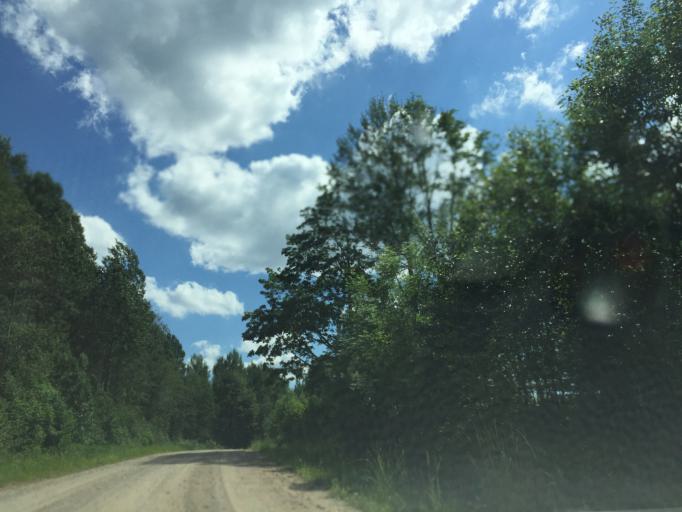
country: LV
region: Priekuli
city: Priekuli
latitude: 57.2475
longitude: 25.4374
